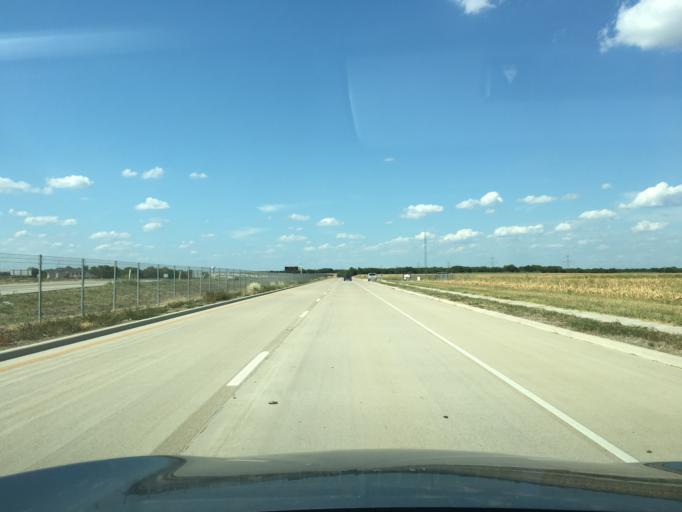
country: US
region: Texas
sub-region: Tarrant County
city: Mansfield
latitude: 32.5327
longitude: -97.0812
